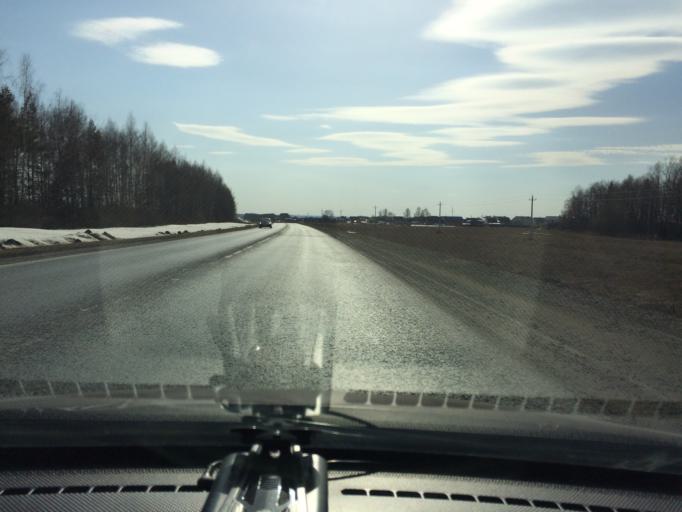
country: RU
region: Mariy-El
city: Yoshkar-Ola
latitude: 56.7179
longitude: 48.0989
